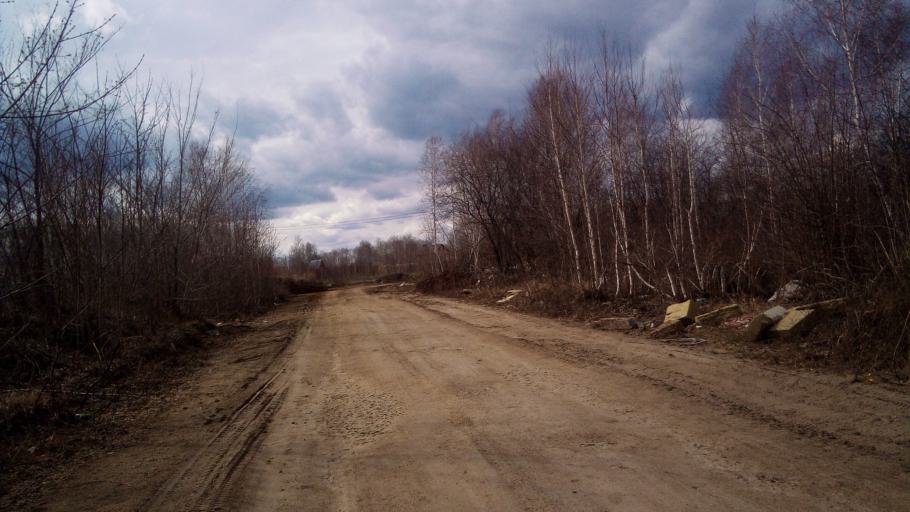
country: RU
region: Chelyabinsk
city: Sargazy
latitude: 55.1266
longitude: 61.2554
